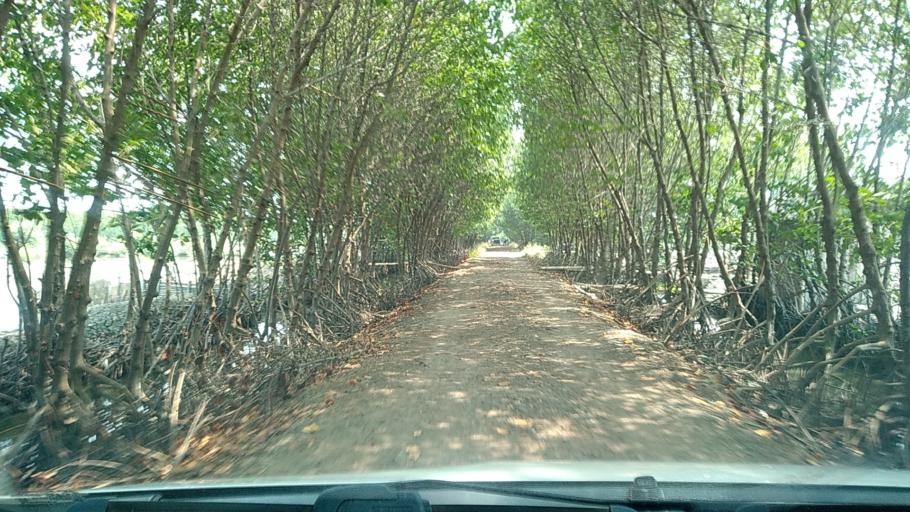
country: ID
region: Central Java
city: Semarang
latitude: -6.9729
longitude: 110.3533
